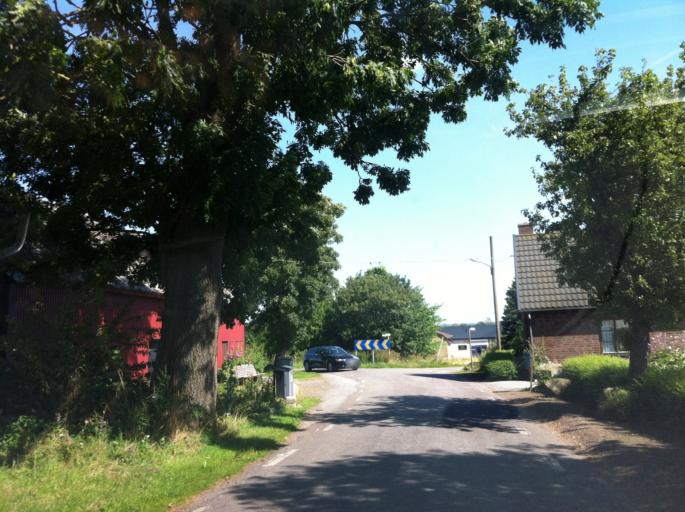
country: SE
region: Skane
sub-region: Helsingborg
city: Glumslov
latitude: 55.9497
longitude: 12.8356
